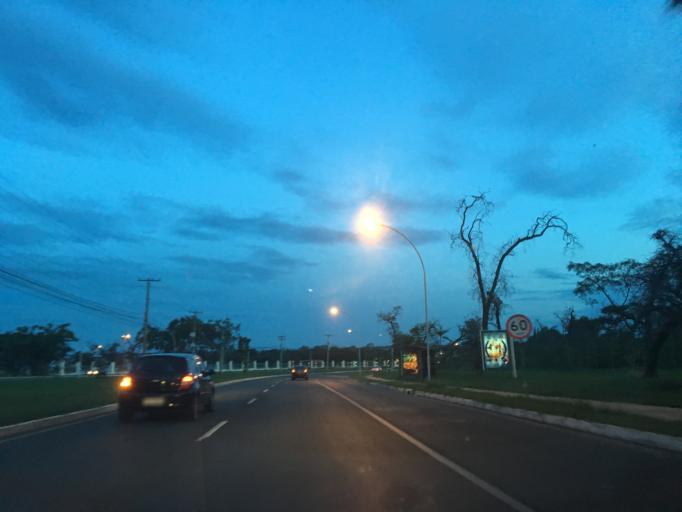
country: BR
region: Federal District
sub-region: Brasilia
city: Brasilia
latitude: -15.8268
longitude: -47.8744
